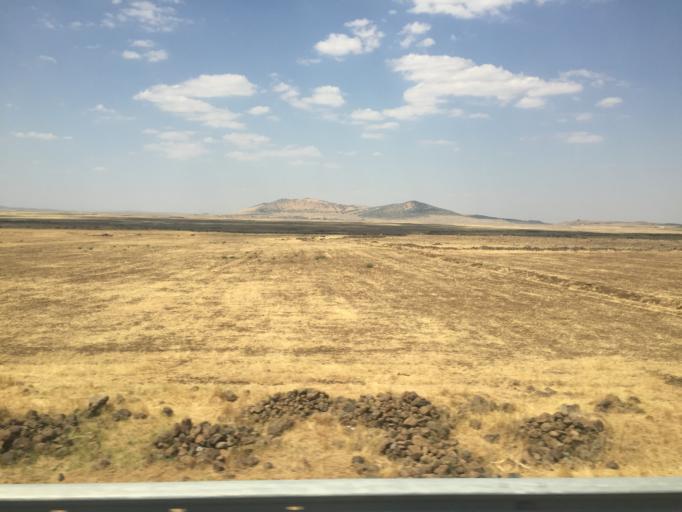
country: TR
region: Sanliurfa
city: Karacadag
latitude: 37.8459
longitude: 39.7075
